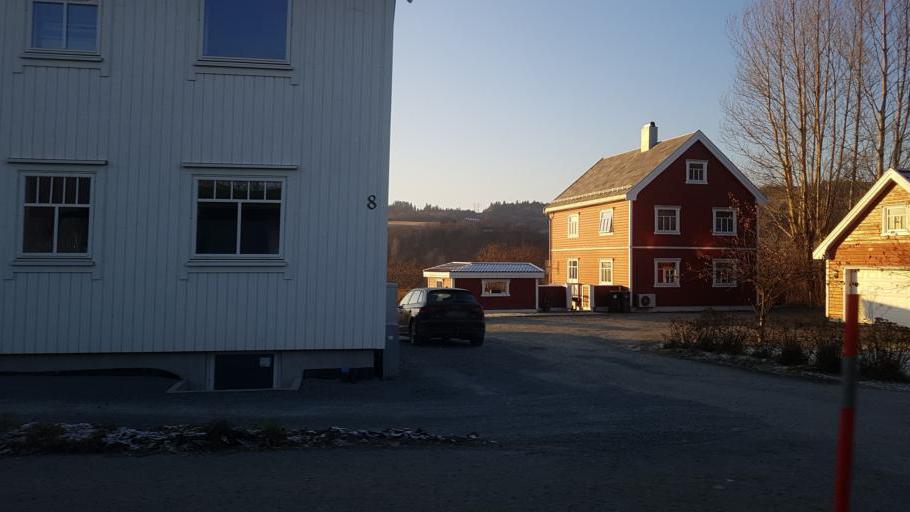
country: NO
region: Sor-Trondelag
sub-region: Melhus
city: Melhus
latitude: 63.2993
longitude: 10.2847
